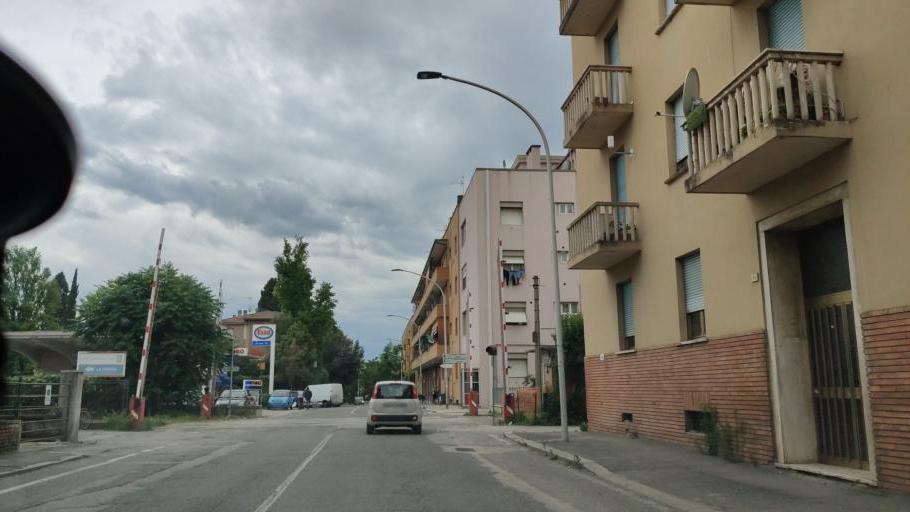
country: IT
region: Umbria
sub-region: Provincia di Terni
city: Terni
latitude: 42.5677
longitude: 12.6585
